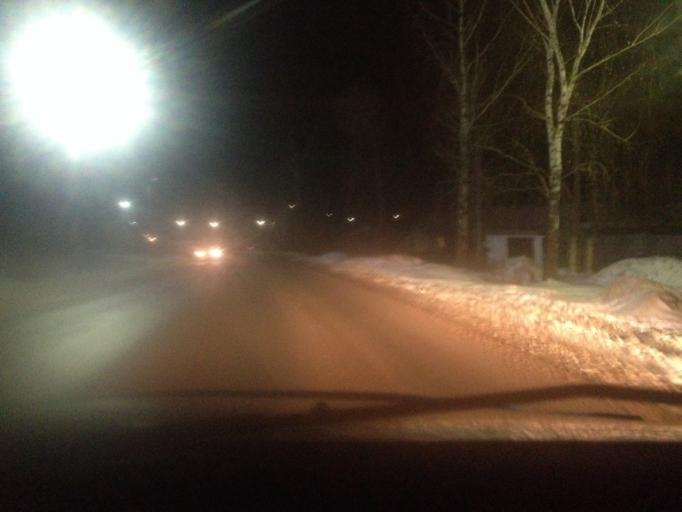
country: RU
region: Tula
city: Leninskiy
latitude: 54.2805
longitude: 37.4565
